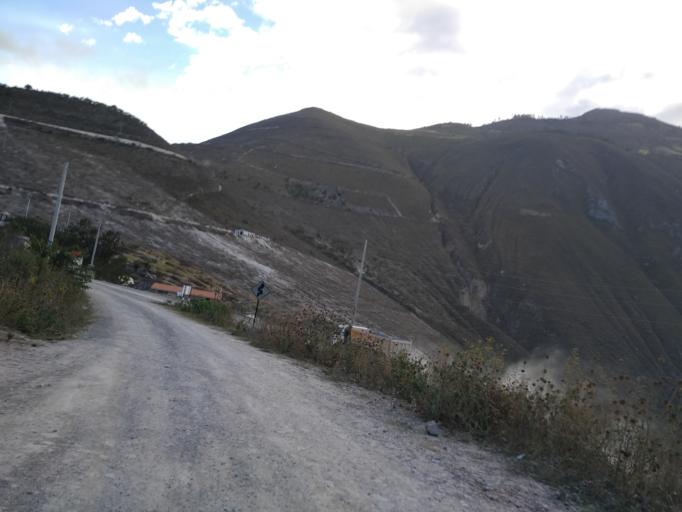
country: PE
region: Amazonas
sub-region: Provincia de Luya
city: Tingo
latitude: -6.3722
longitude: -77.9122
